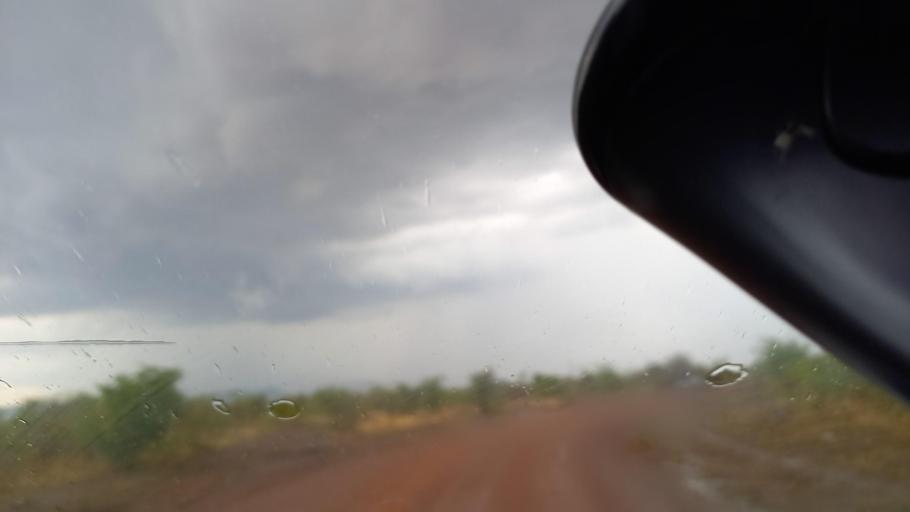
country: ZM
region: Lusaka
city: Kafue
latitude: -15.8639
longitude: 28.1774
